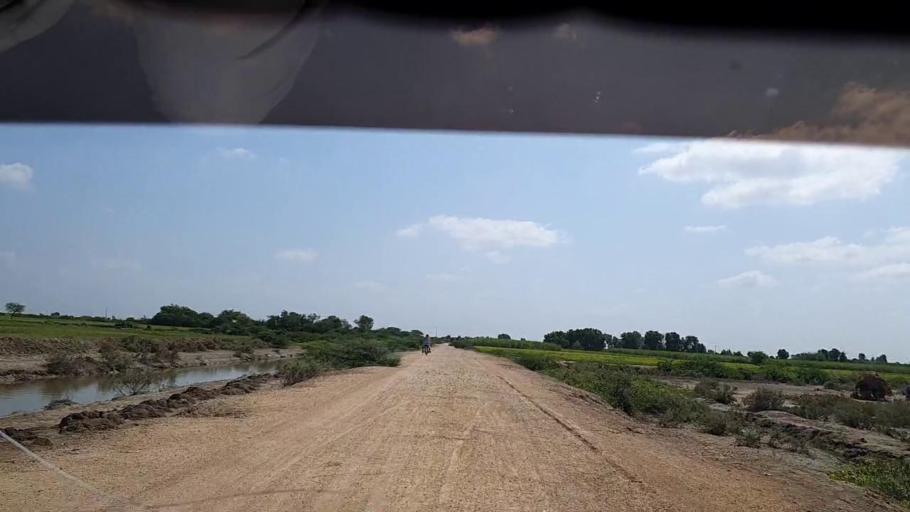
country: PK
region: Sindh
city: Kadhan
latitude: 24.5927
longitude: 68.9920
